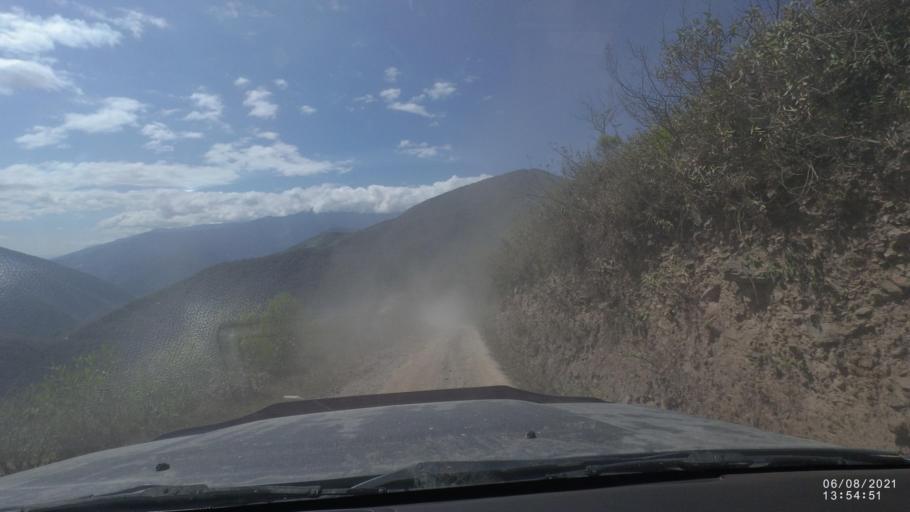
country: BO
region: La Paz
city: Quime
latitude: -16.6489
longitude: -66.7314
